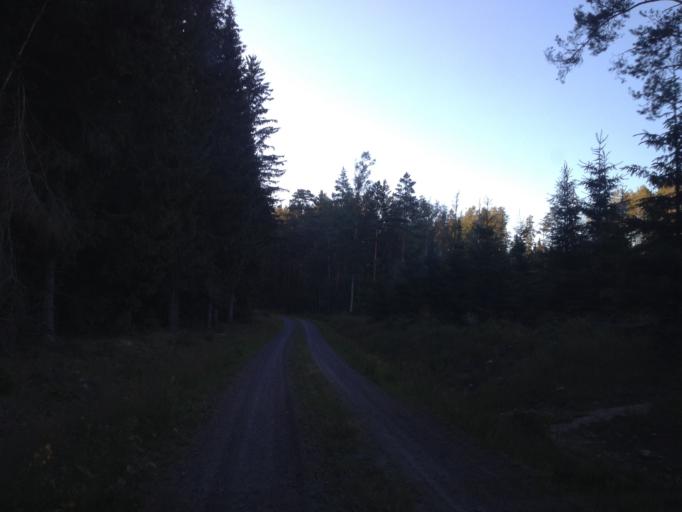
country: SE
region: Kalmar
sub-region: Vasterviks Kommun
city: Overum
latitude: 58.0041
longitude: 16.1220
